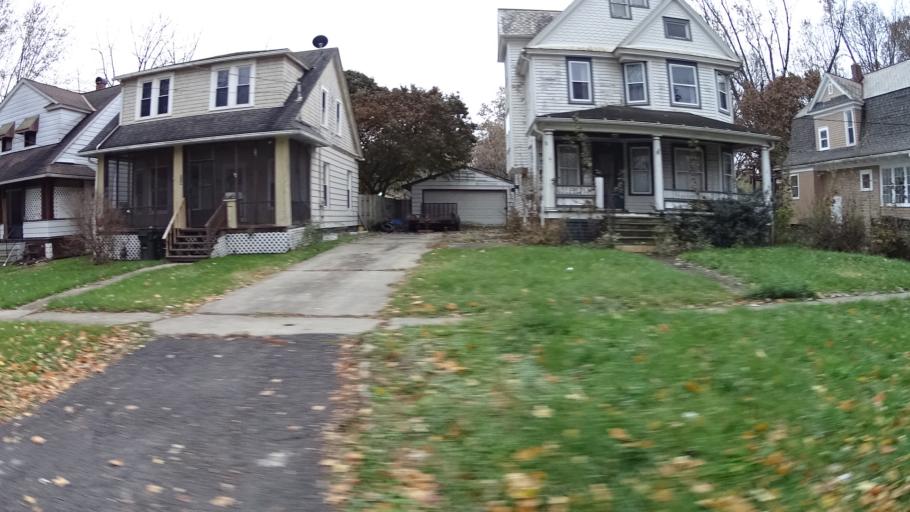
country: US
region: Ohio
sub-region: Lorain County
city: Elyria
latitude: 41.3586
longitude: -82.1052
